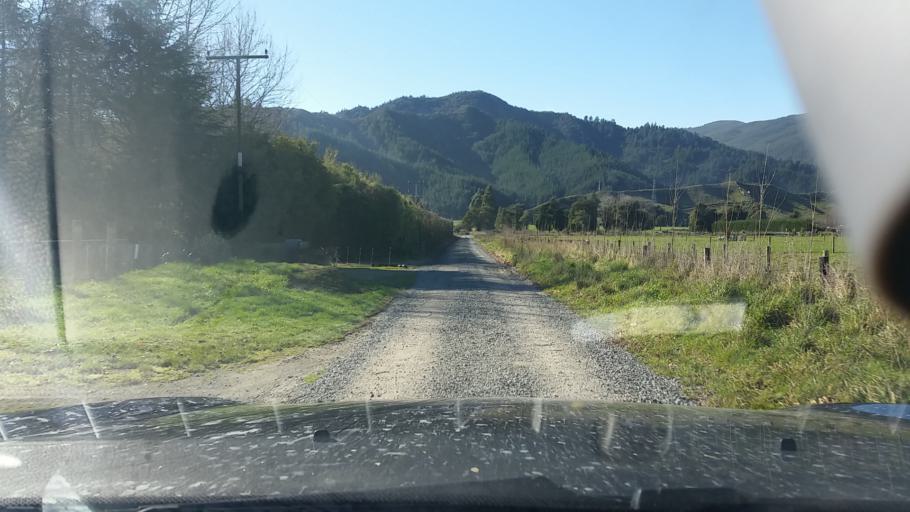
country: NZ
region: Marlborough
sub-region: Marlborough District
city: Blenheim
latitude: -41.4322
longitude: 173.7614
